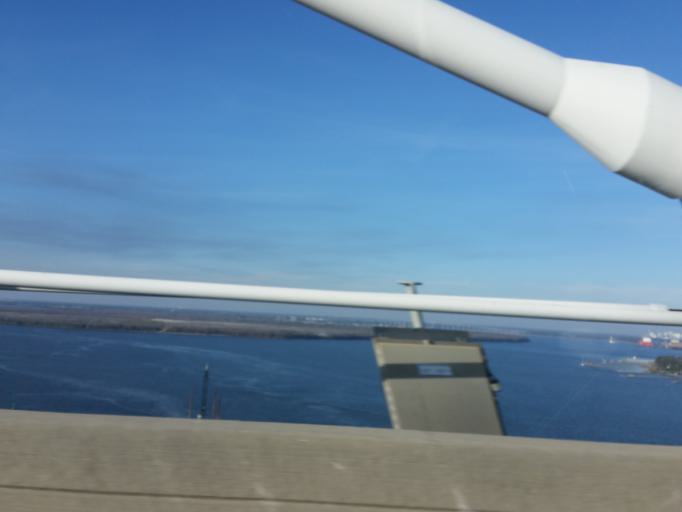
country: US
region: South Carolina
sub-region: Charleston County
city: Charleston
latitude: 32.8030
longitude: -79.9151
